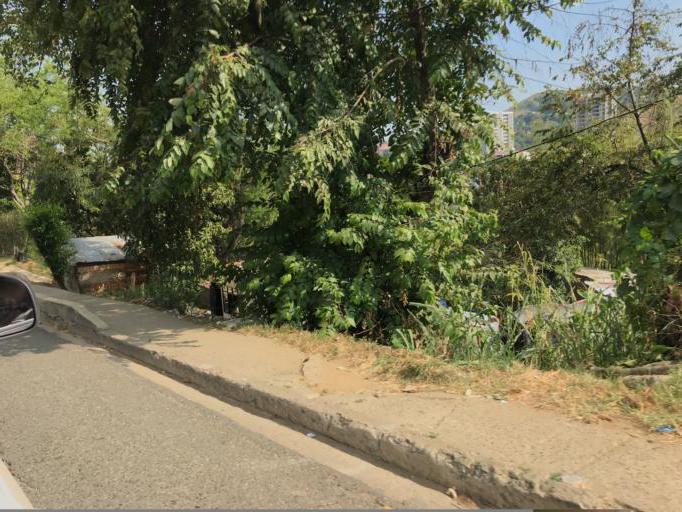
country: CO
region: Valle del Cauca
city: Cali
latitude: 3.4508
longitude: -76.5607
